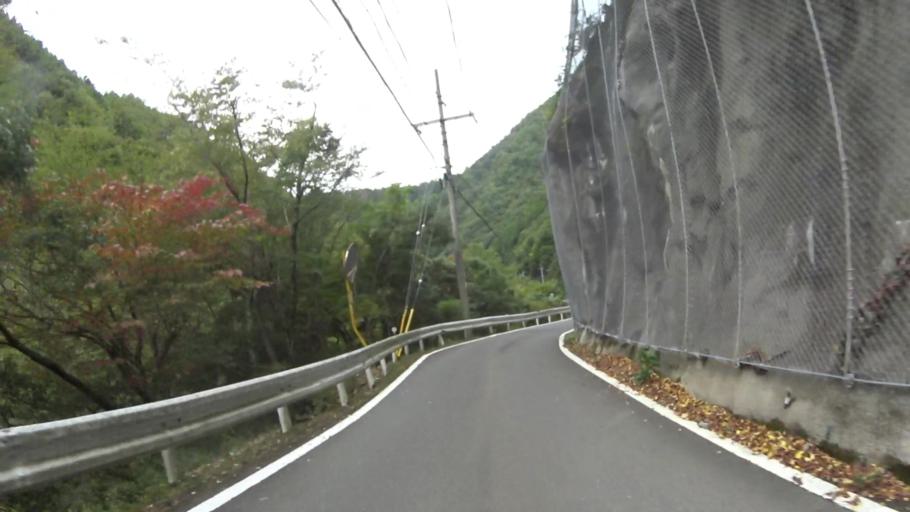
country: JP
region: Fukui
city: Obama
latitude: 35.3076
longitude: 135.6935
